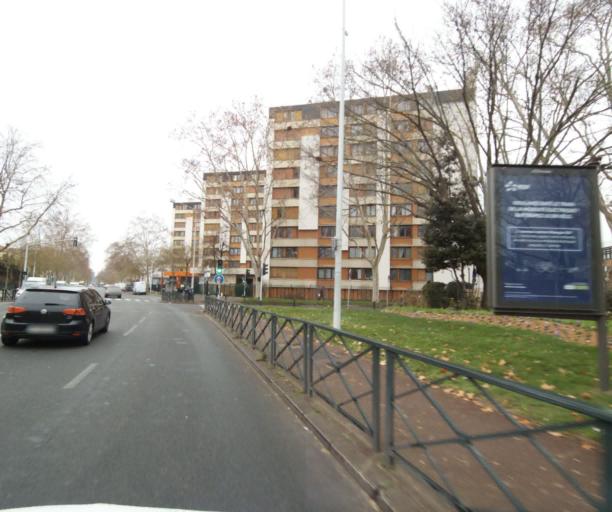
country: FR
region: Ile-de-France
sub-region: Departement des Hauts-de-Seine
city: Rueil-Malmaison
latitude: 48.8883
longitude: 2.1939
